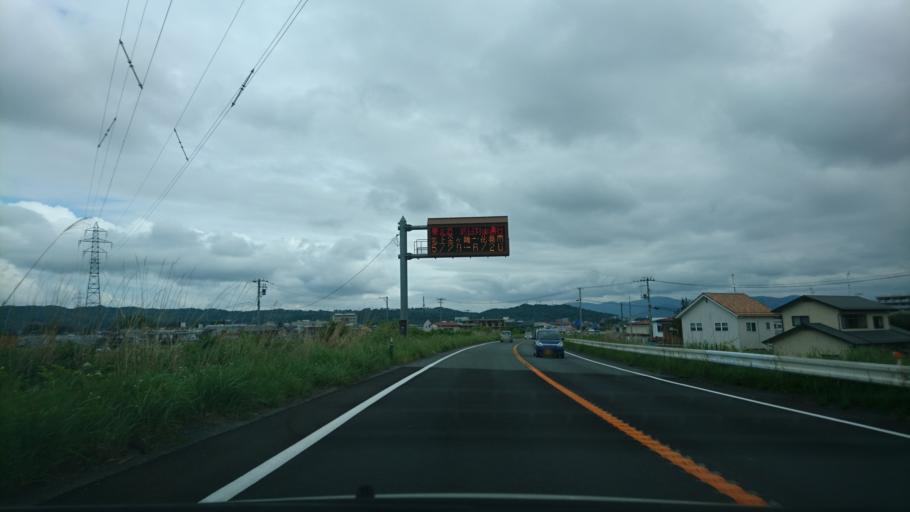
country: JP
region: Iwate
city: Ichinoseki
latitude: 38.9169
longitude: 141.1076
